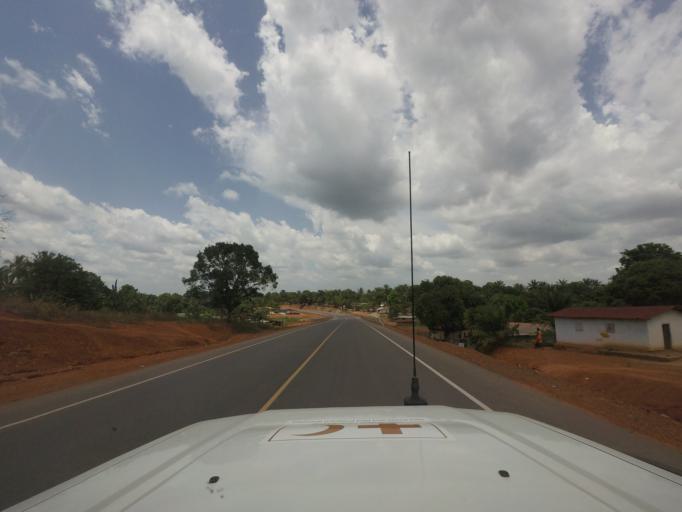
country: LR
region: Nimba
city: Sanniquellie
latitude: 7.2403
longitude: -8.9818
